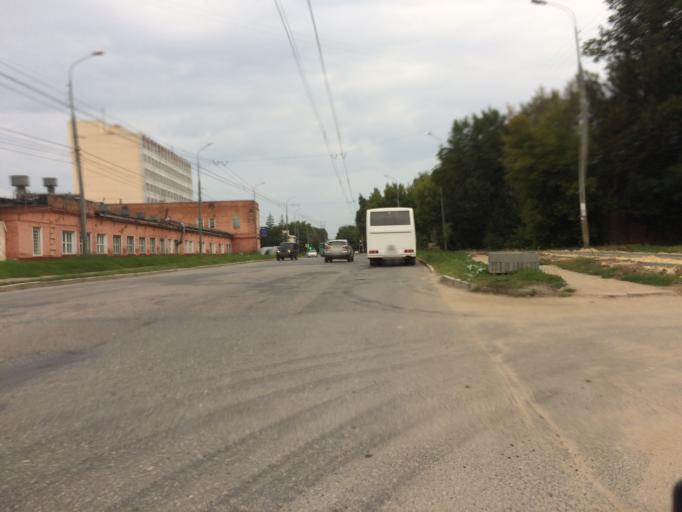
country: RU
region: Mariy-El
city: Yoshkar-Ola
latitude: 56.6330
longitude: 47.8691
